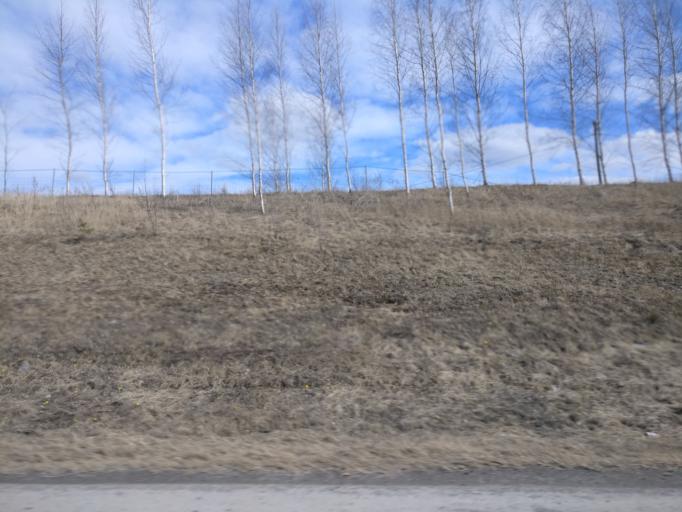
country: FI
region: Pirkanmaa
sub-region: Tampere
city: Lempaeaelae
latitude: 61.3479
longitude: 23.7896
